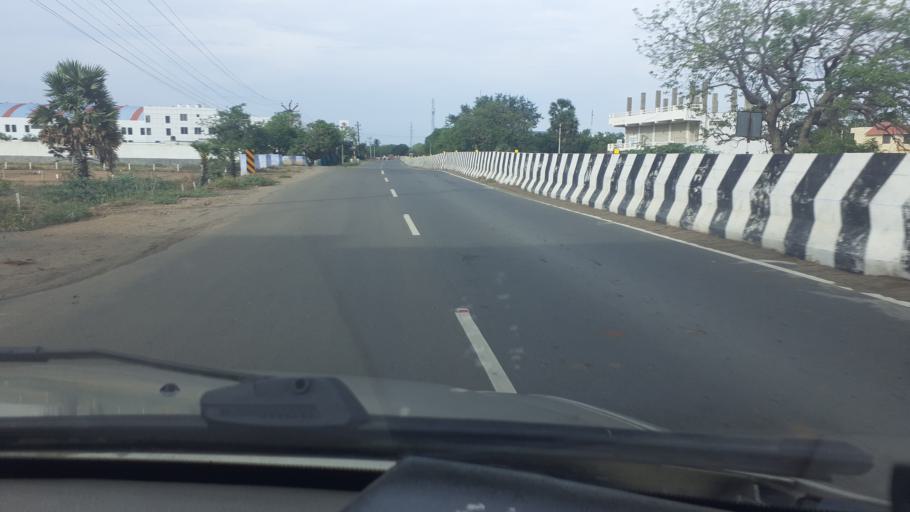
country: IN
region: Tamil Nadu
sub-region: Tirunelveli Kattabo
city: Tirunelveli
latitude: 8.6667
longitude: 77.7169
